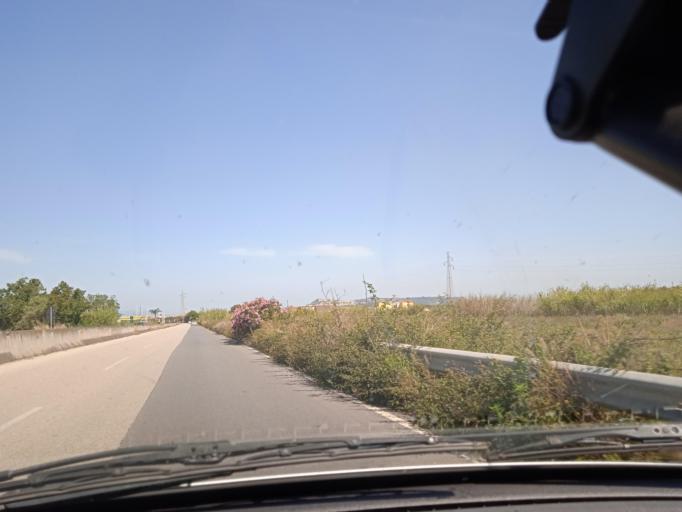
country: IT
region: Sicily
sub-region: Messina
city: San Filippo del Mela
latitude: 38.1899
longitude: 15.2613
